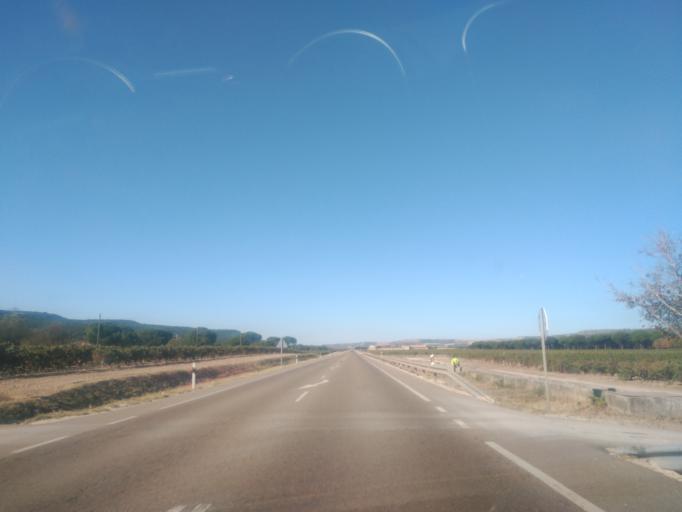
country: ES
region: Castille and Leon
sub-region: Provincia de Valladolid
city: Valbuena de Duero
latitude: 41.6284
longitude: -4.3007
